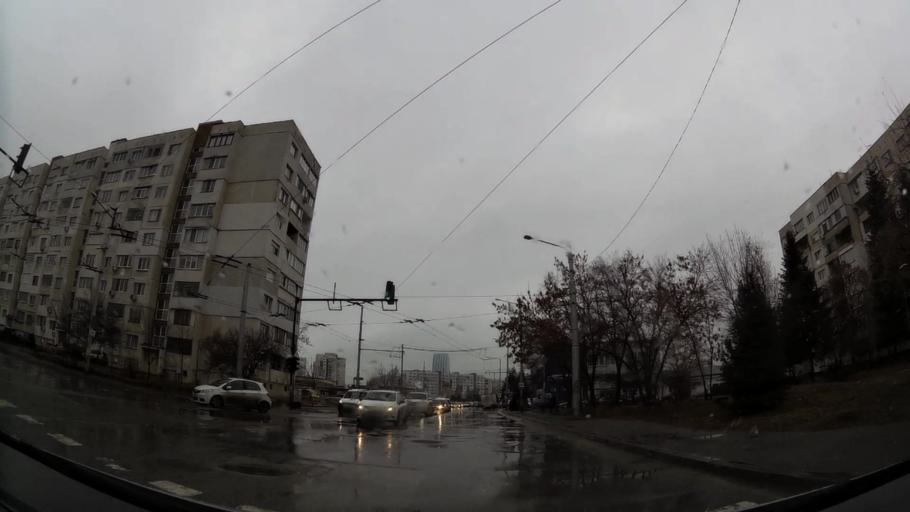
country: BG
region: Sofia-Capital
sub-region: Stolichna Obshtina
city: Sofia
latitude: 42.6578
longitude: 23.4019
